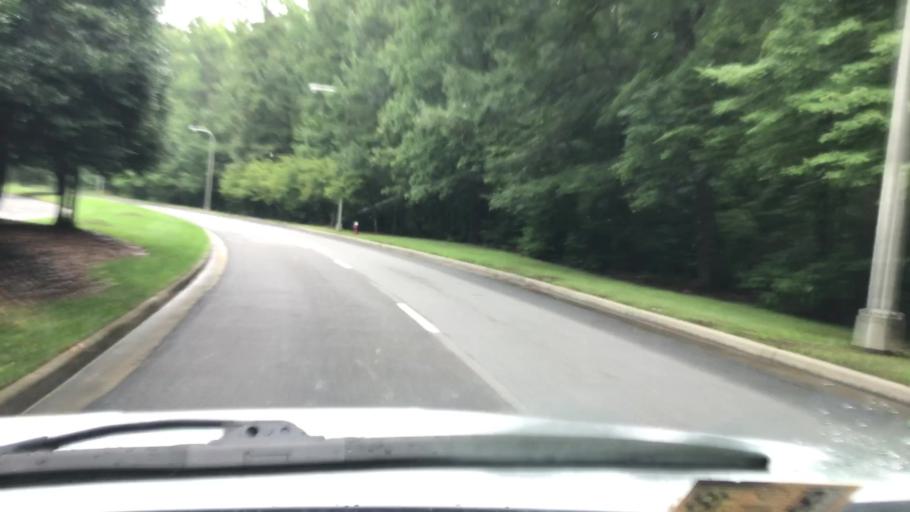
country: US
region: Virginia
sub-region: Henrico County
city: Short Pump
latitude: 37.6064
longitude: -77.6712
